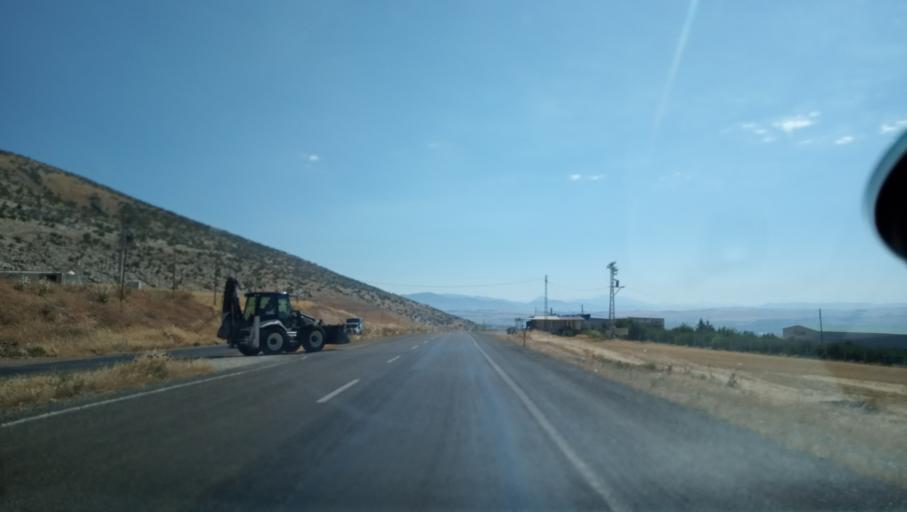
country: TR
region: Diyarbakir
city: Malabadi
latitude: 38.1236
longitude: 41.1578
